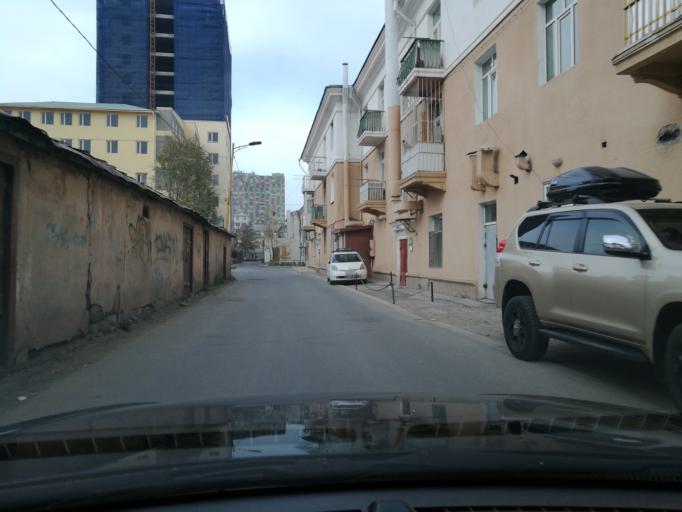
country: MN
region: Ulaanbaatar
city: Ulaanbaatar
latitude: 47.9229
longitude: 106.9179
